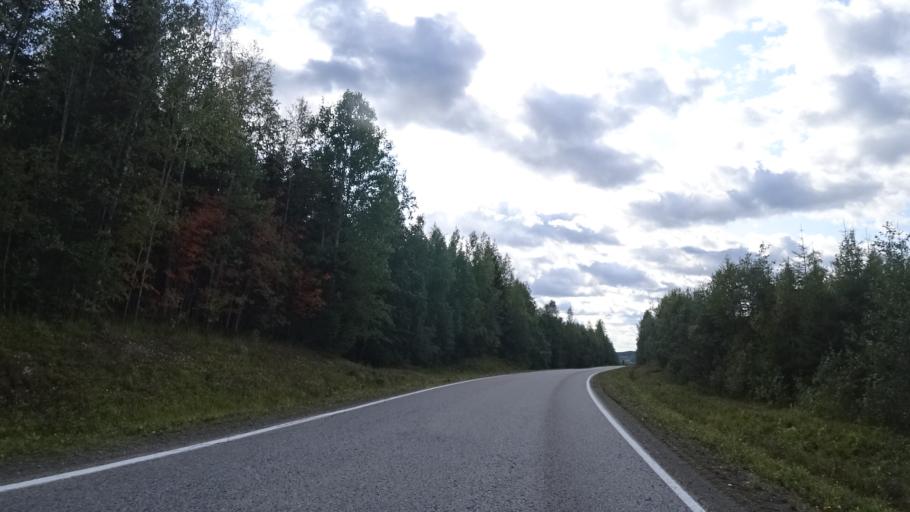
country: RU
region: Republic of Karelia
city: Vyartsilya
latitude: 62.2245
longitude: 30.6576
